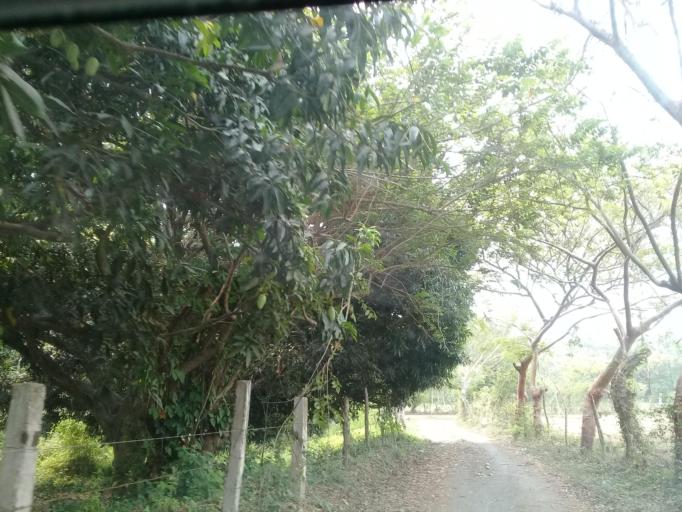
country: MX
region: Veracruz
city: El Tejar
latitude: 19.0523
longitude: -96.1957
